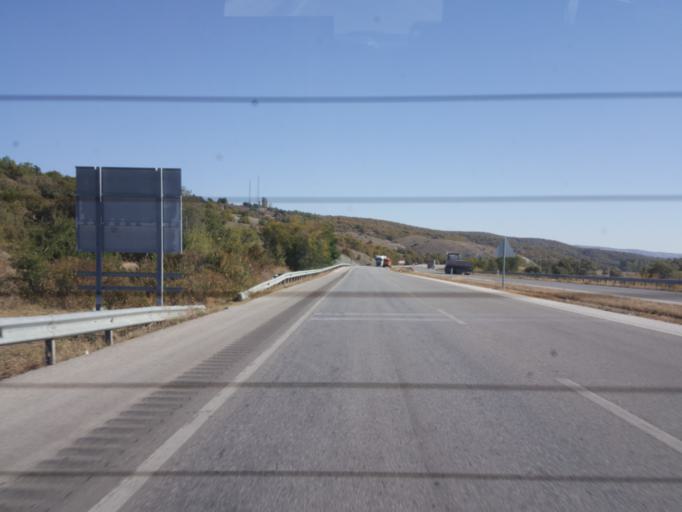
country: TR
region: Corum
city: Alaca
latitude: 40.3101
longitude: 34.6585
